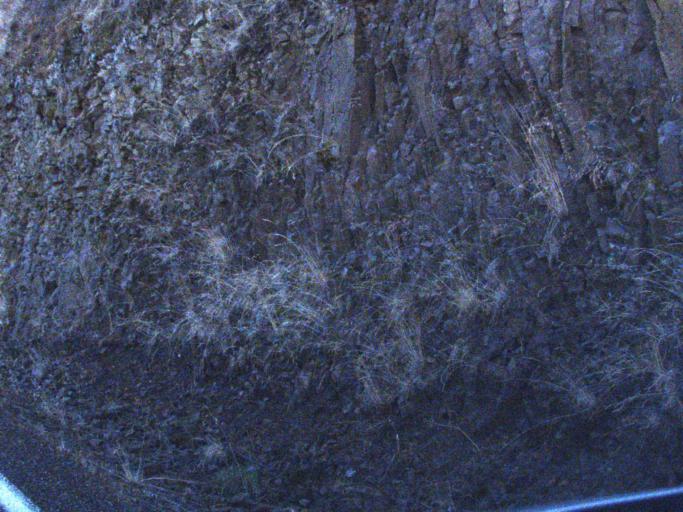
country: US
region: Washington
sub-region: Asotin County
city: Asotin
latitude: 46.0662
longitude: -117.2279
